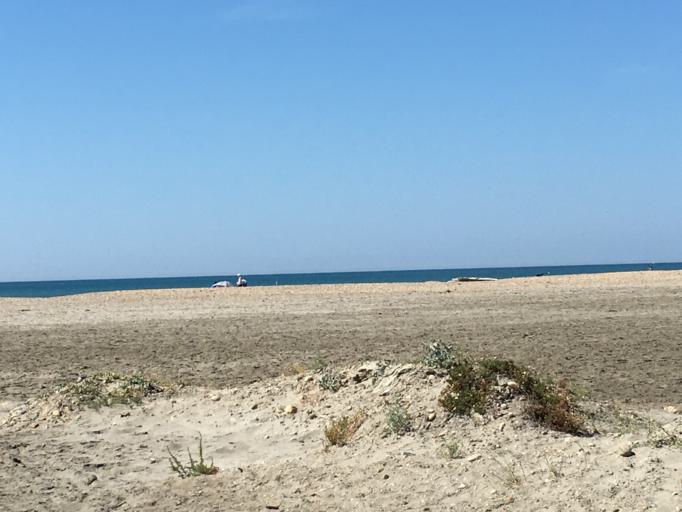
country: FR
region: Provence-Alpes-Cote d'Azur
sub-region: Departement des Bouches-du-Rhone
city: Saintes-Maries-de-la-Mer
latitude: 43.4592
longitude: 4.4583
